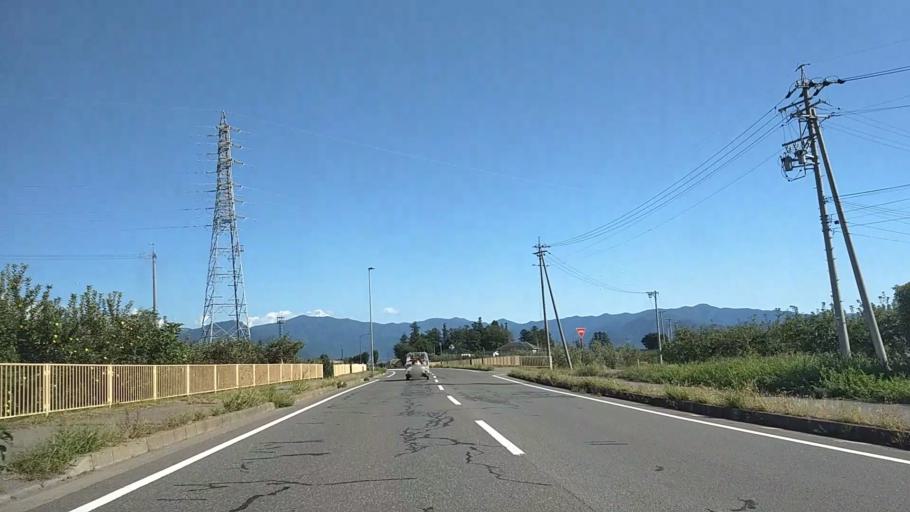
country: JP
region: Nagano
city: Nagano-shi
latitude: 36.6150
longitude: 138.1377
